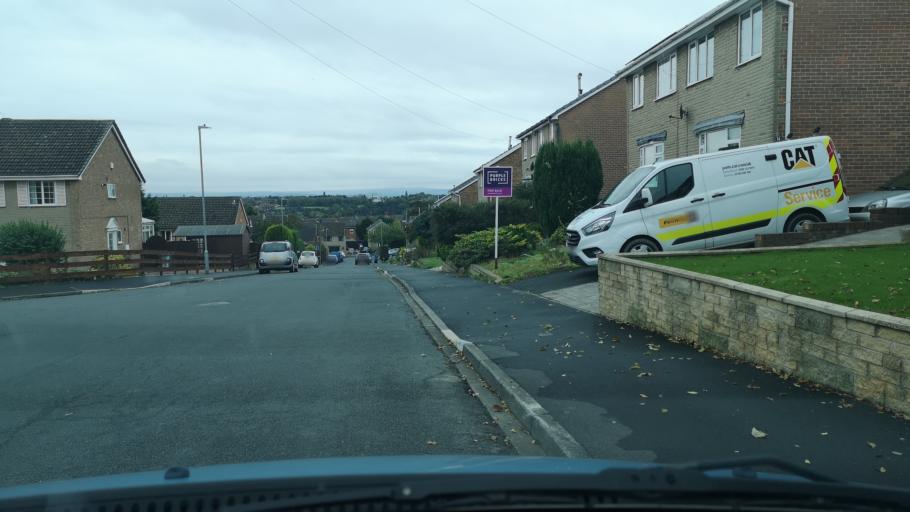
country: GB
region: England
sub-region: City and Borough of Leeds
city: Drighlington
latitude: 53.7353
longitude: -1.6539
